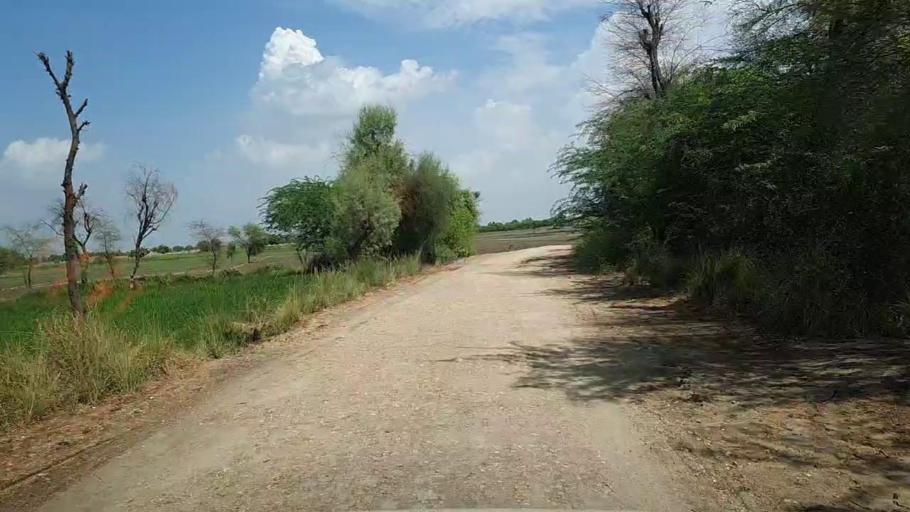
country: PK
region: Sindh
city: Bhiria
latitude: 26.9213
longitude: 68.2262
